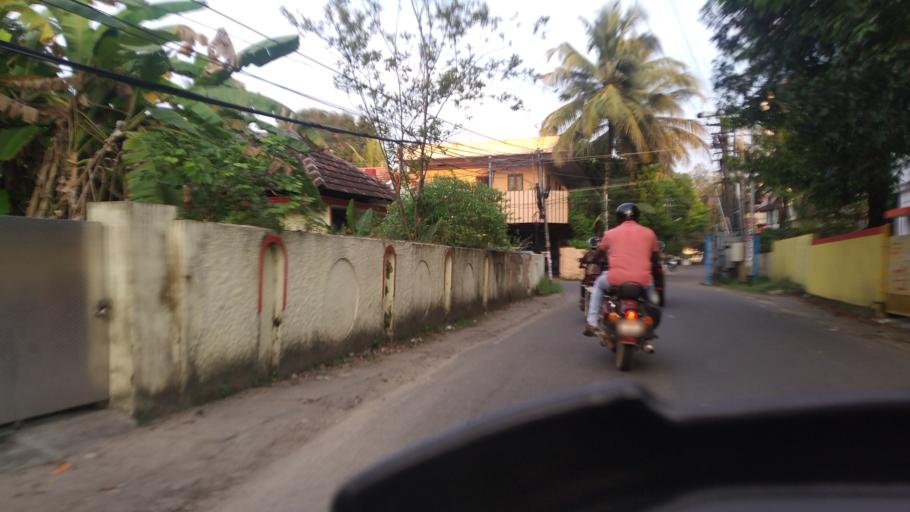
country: IN
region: Kerala
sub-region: Ernakulam
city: Elur
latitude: 10.0200
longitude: 76.3003
